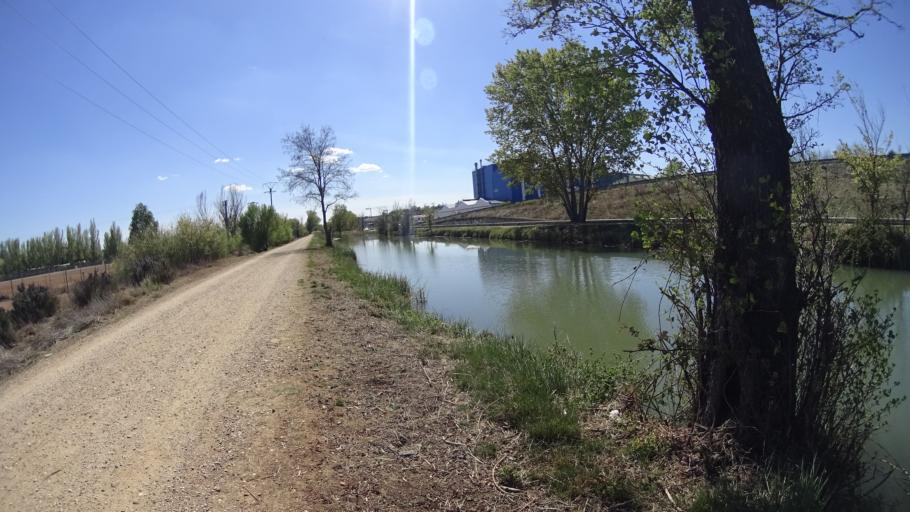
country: ES
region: Castille and Leon
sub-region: Provincia de Valladolid
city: Santovenia de Pisuerga
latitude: 41.7006
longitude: -4.7111
